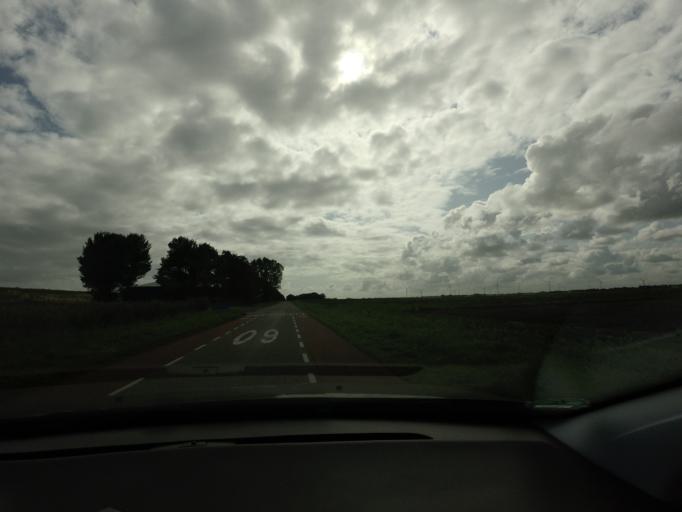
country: NL
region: North Holland
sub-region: Gemeente Medemblik
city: Medemblik
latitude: 52.8622
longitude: 5.0989
